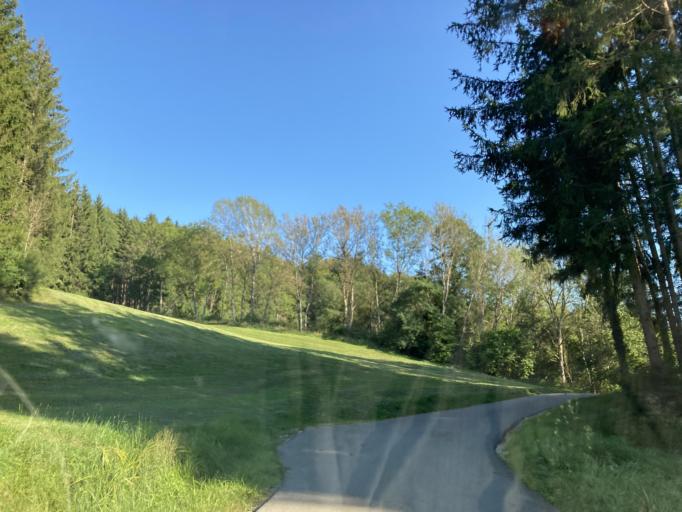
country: DE
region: Baden-Wuerttemberg
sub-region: Freiburg Region
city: Blumberg
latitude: 47.8289
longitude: 8.5083
